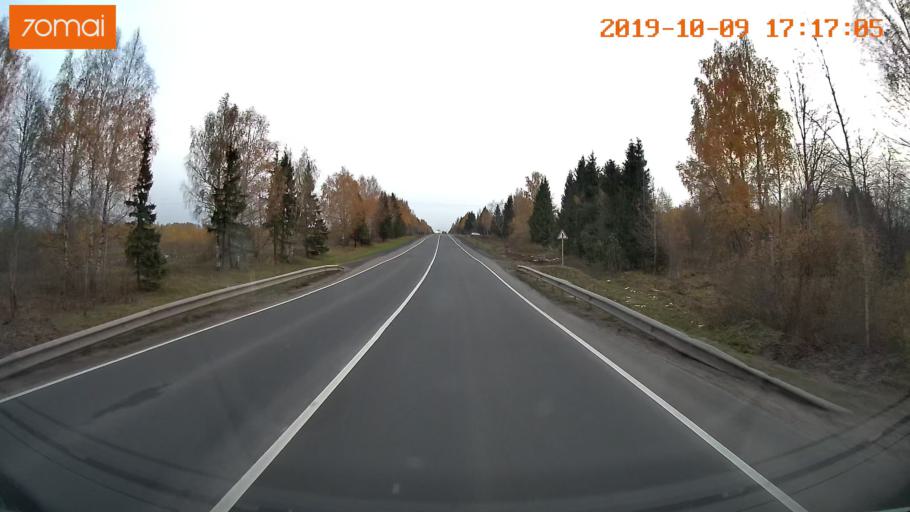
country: RU
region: Ivanovo
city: Furmanov
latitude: 57.2807
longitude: 41.1590
